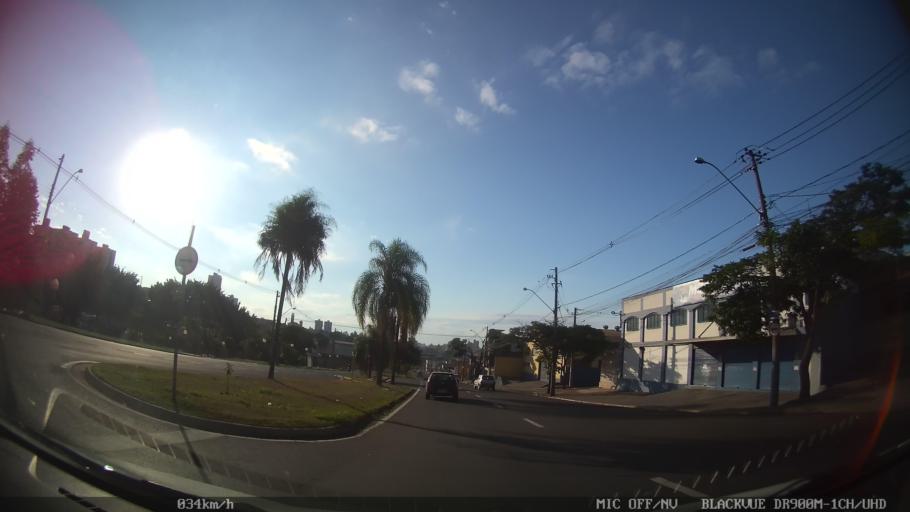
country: BR
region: Sao Paulo
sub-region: Piracicaba
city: Piracicaba
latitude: -22.7539
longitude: -47.6431
